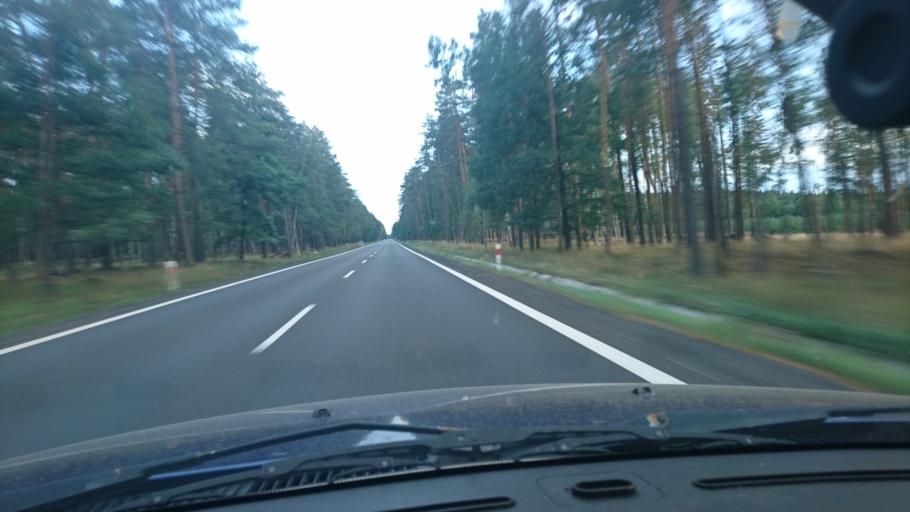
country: PL
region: Silesian Voivodeship
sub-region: Powiat tarnogorski
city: Tworog
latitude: 50.5659
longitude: 18.7121
